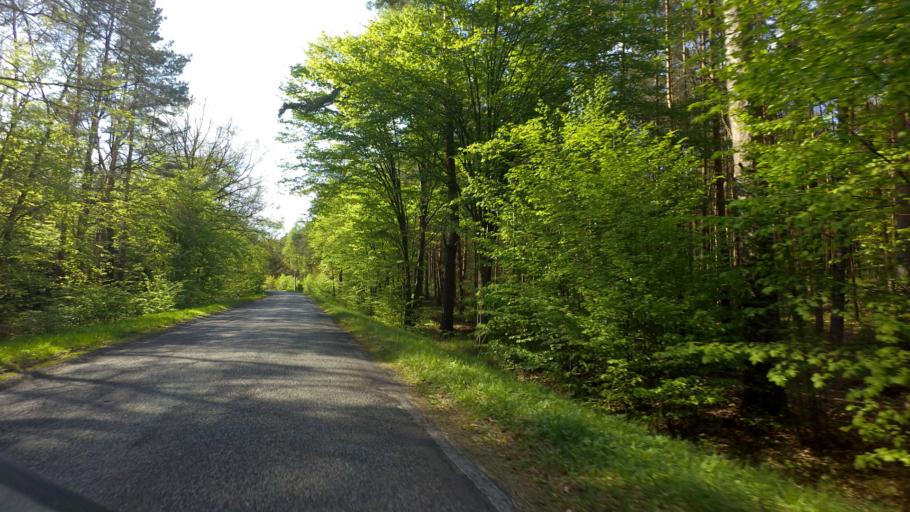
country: DE
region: Brandenburg
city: Zehdenick
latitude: 53.0163
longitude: 13.4124
